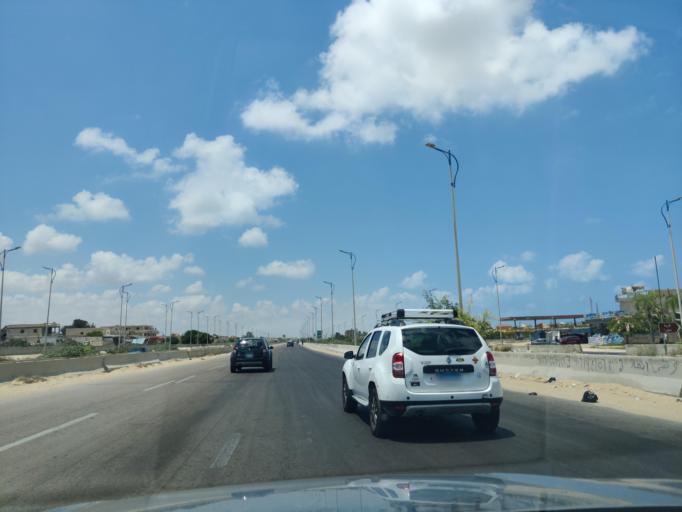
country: EG
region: Alexandria
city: Alexandria
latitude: 31.0038
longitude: 29.6159
